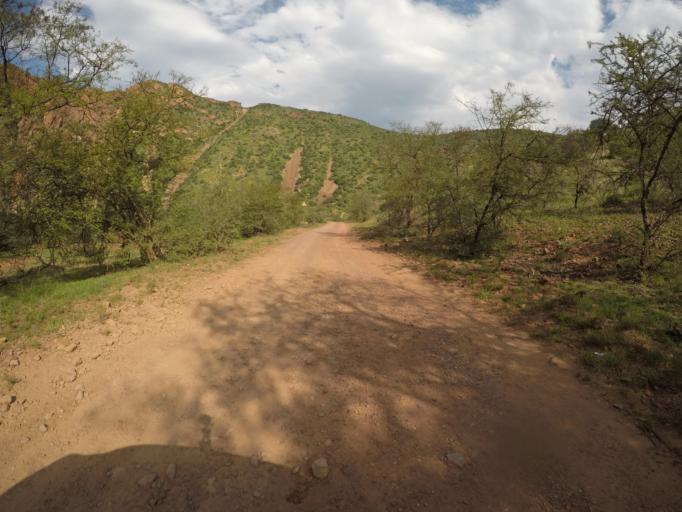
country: ZA
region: Eastern Cape
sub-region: Cacadu District Municipality
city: Kareedouw
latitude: -33.6409
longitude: 24.3172
